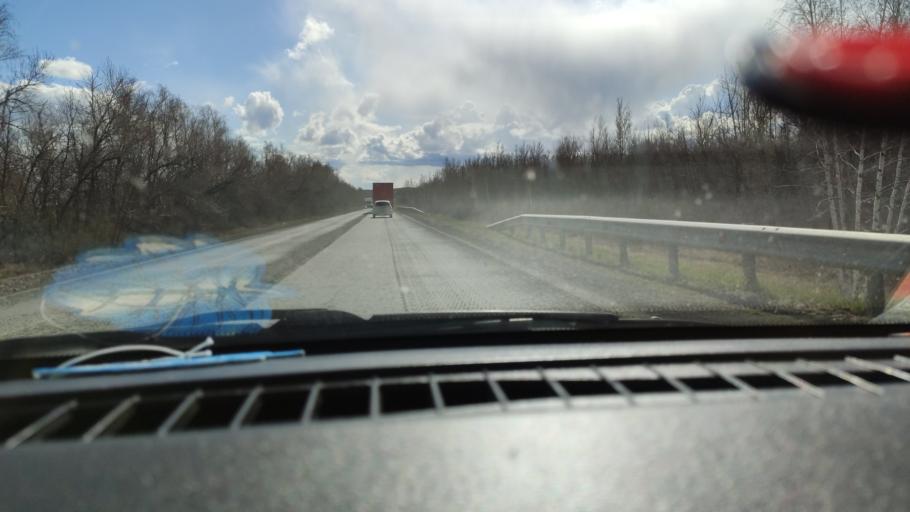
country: RU
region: Saratov
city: Dukhovnitskoye
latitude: 52.6688
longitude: 48.2193
